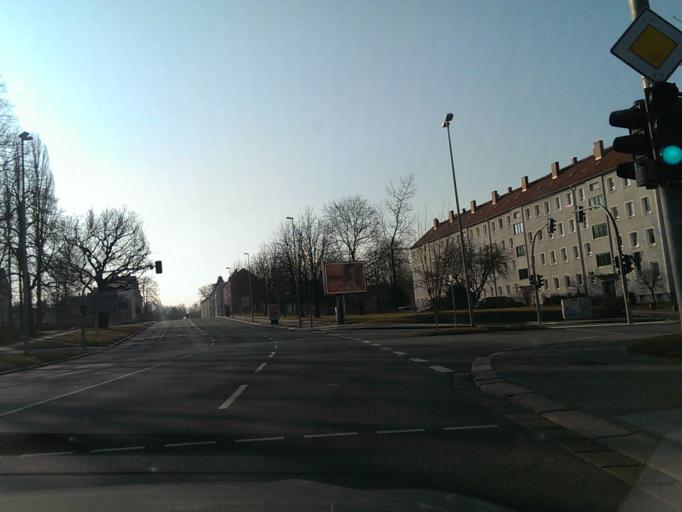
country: DE
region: Saxony
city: Chemnitz
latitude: 50.8267
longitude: 12.9287
